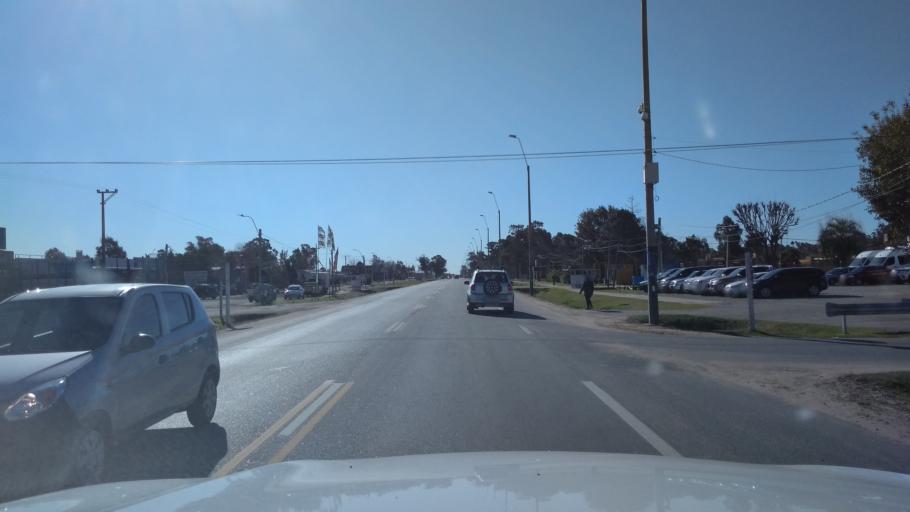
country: UY
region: Canelones
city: Atlantida
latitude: -34.7617
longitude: -55.7654
